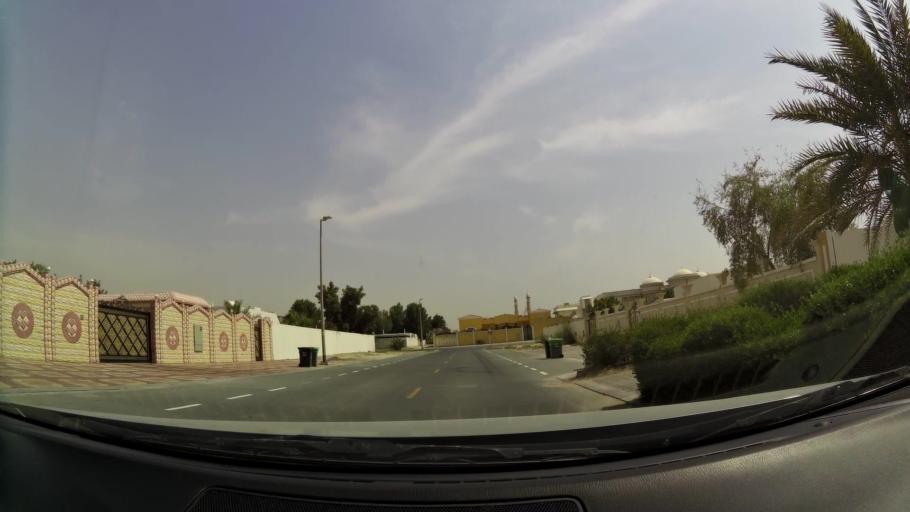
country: AE
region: Ash Shariqah
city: Sharjah
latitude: 25.2415
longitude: 55.4409
